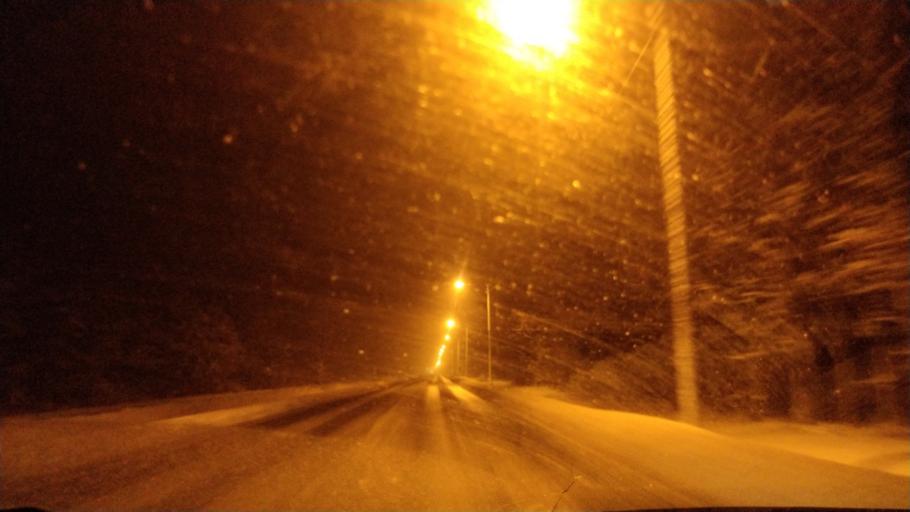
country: FI
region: Lapland
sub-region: Rovaniemi
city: Rovaniemi
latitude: 66.4132
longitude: 25.4083
